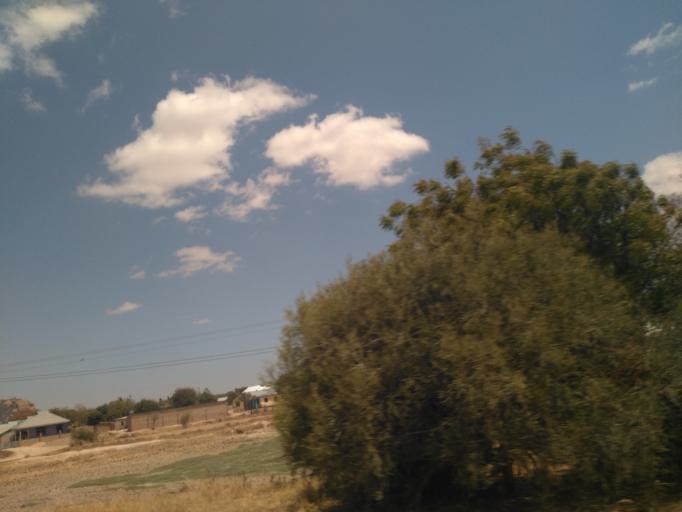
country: TZ
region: Dodoma
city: Kisasa
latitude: -6.1649
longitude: 35.7866
